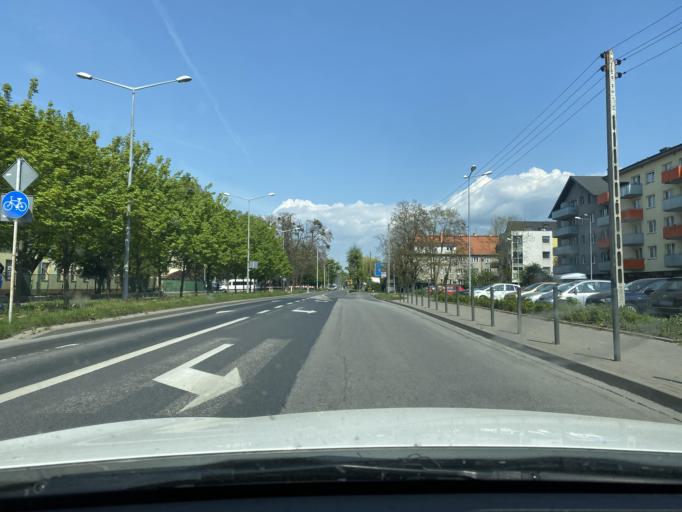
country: PL
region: Lower Silesian Voivodeship
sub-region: Powiat wroclawski
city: Wroclaw
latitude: 51.1423
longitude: 17.0259
